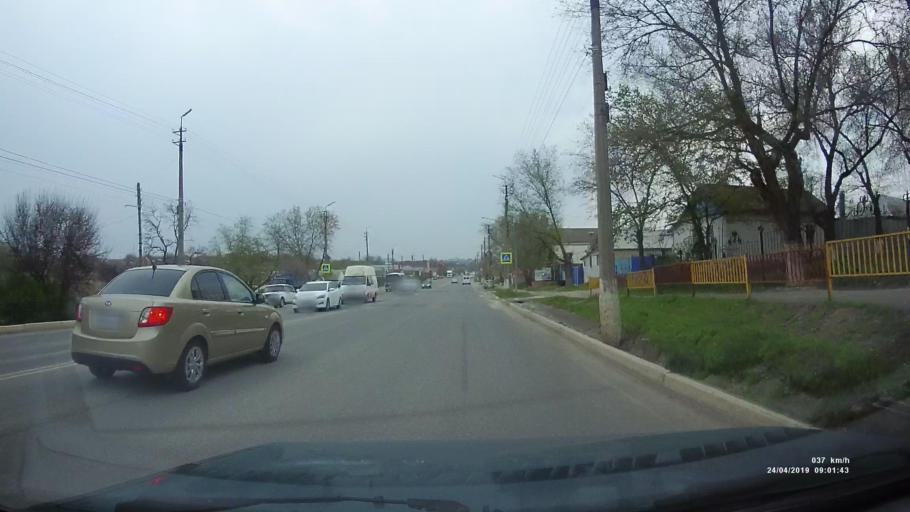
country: RU
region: Kalmykiya
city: Elista
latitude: 46.3126
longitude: 44.2274
